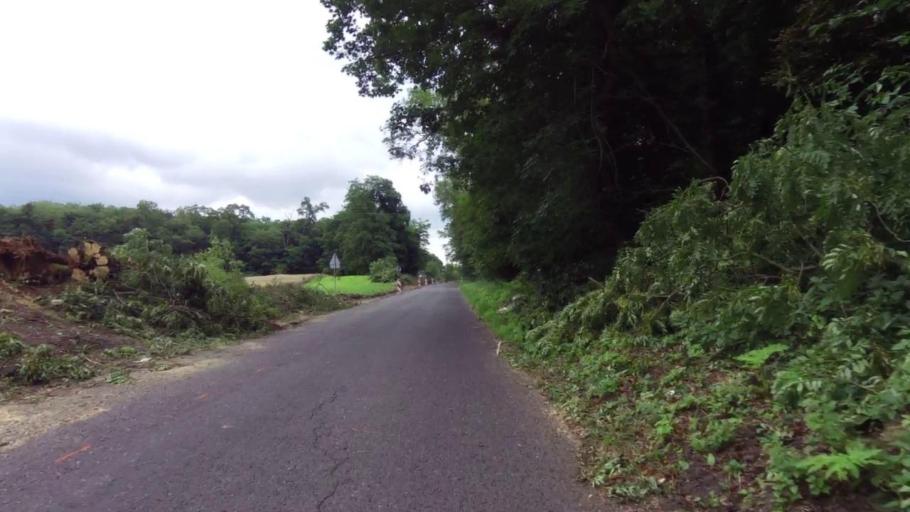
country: PL
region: West Pomeranian Voivodeship
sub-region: Powiat gryfinski
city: Cedynia
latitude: 52.8697
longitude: 14.2273
